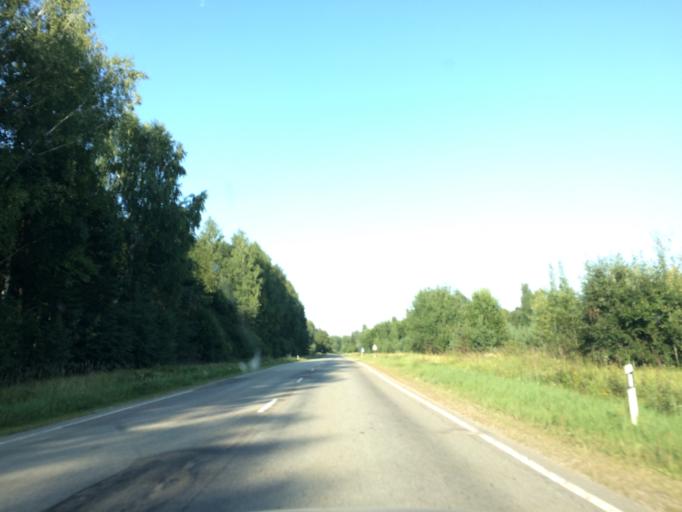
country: LV
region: Ludzas Rajons
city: Ludza
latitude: 56.5369
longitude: 27.5643
